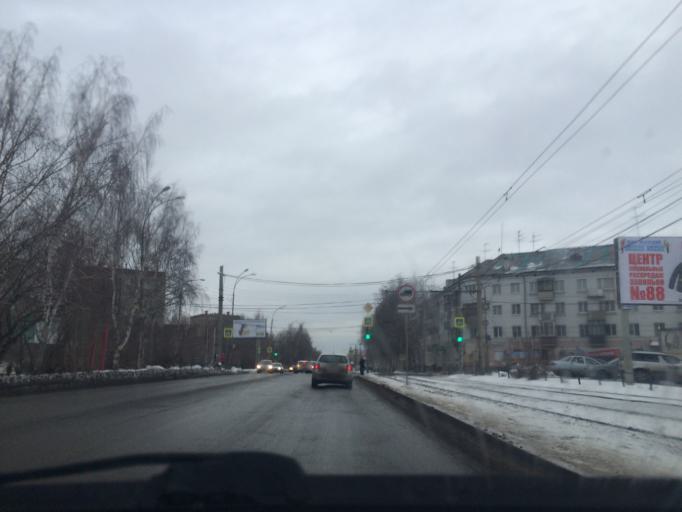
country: RU
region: Sverdlovsk
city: Yekaterinburg
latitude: 56.8569
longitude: 60.6528
